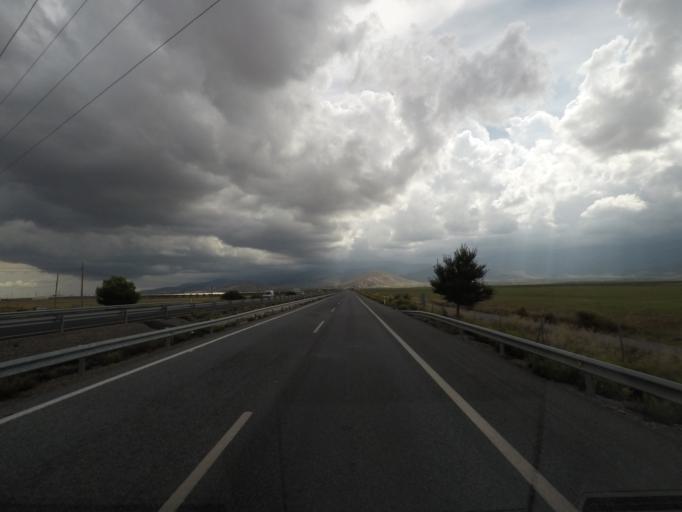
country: ES
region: Andalusia
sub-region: Provincia de Granada
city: Albunan
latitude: 37.2231
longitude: -3.0786
